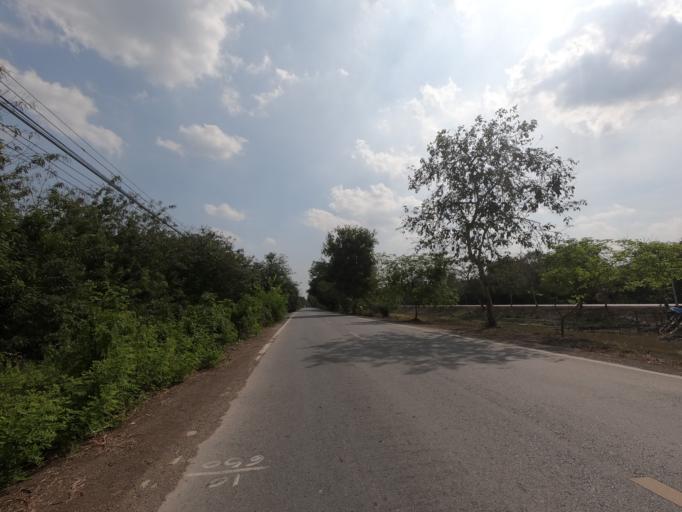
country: TH
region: Pathum Thani
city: Nong Suea
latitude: 14.1571
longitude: 100.8464
